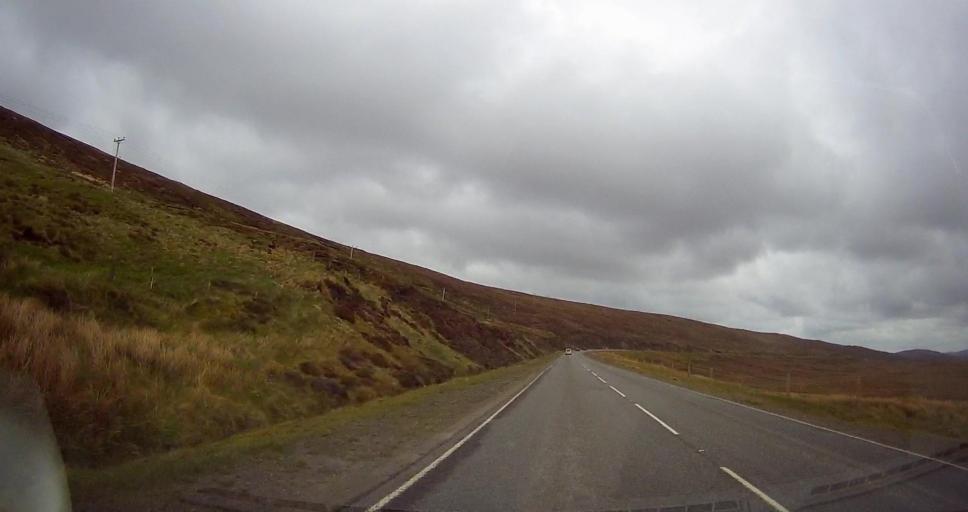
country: GB
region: Scotland
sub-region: Shetland Islands
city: Lerwick
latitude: 60.3079
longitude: -1.2437
